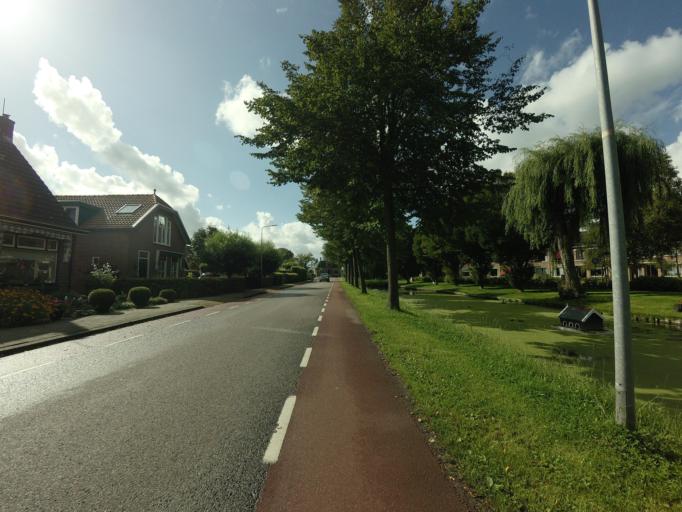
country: NL
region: North Holland
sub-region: Gemeente Hoorn
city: Hoorn
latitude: 52.6417
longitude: 5.0017
